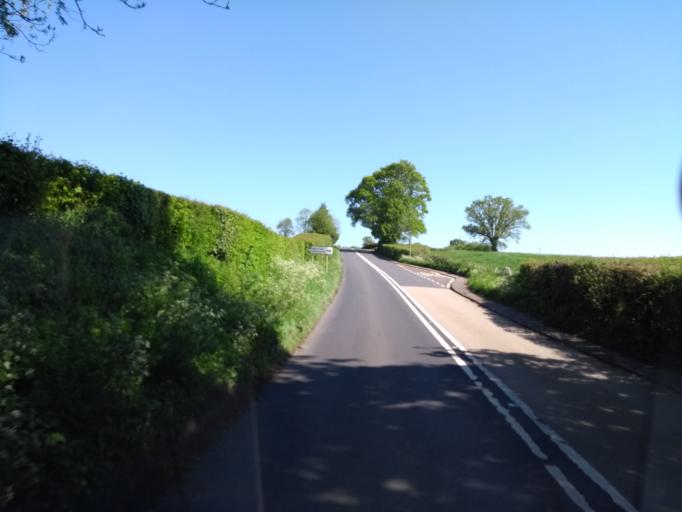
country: GB
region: England
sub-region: Devon
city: Axminster
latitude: 50.8054
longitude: -2.9796
